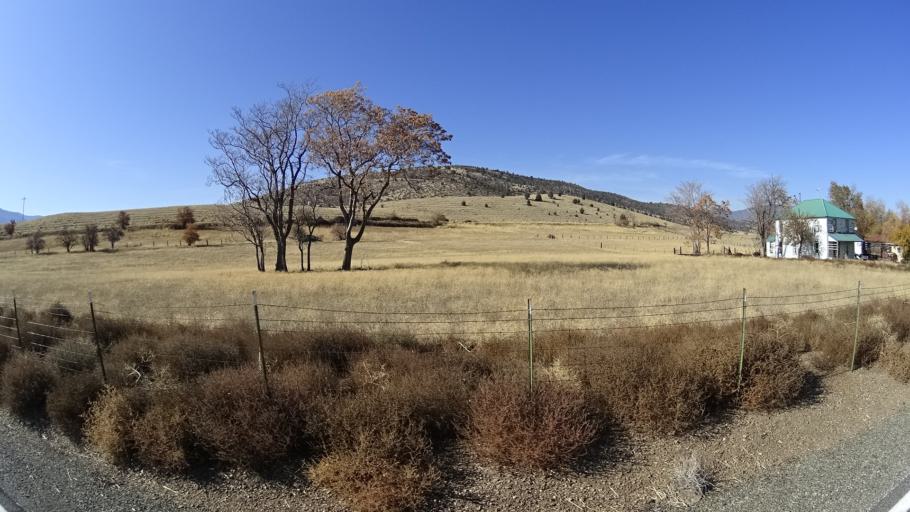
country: US
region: California
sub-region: Siskiyou County
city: Weed
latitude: 41.5139
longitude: -122.5258
